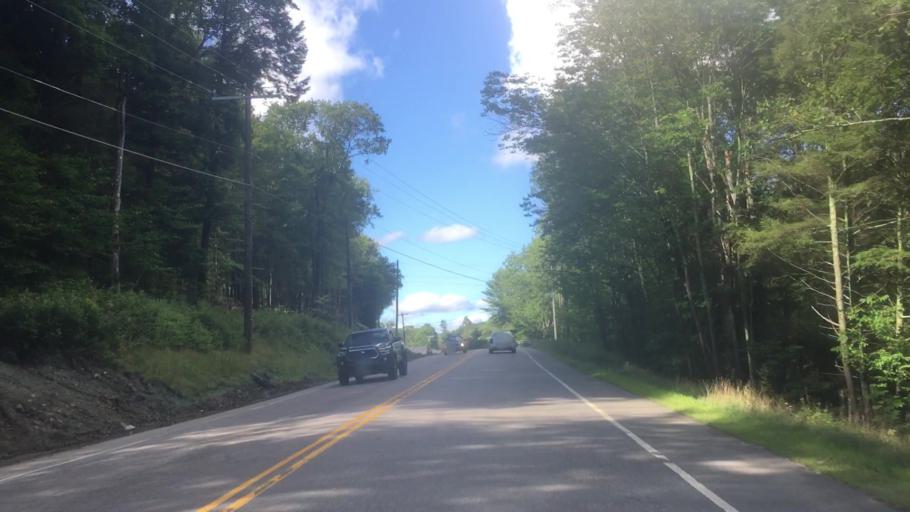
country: US
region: New Hampshire
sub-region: Cheshire County
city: Marlborough
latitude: 42.9894
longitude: -72.1976
